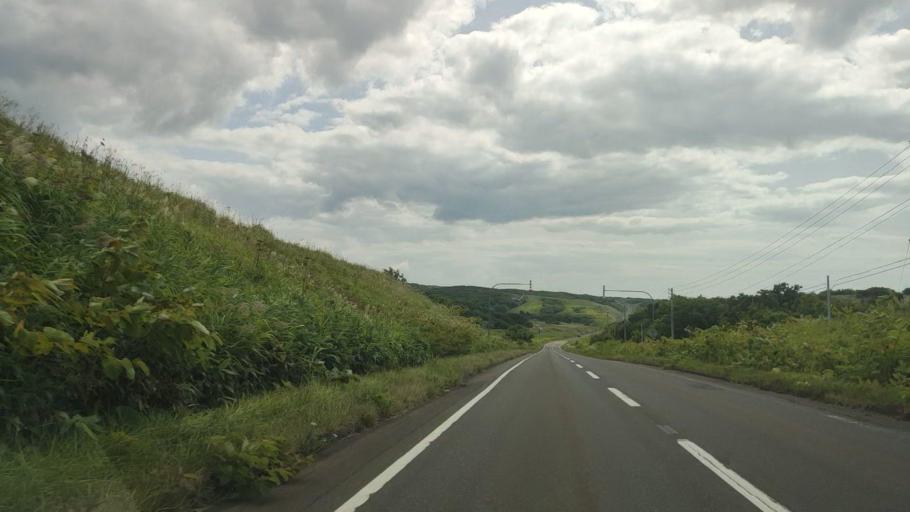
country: JP
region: Hokkaido
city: Rumoi
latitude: 44.5996
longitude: 141.7914
